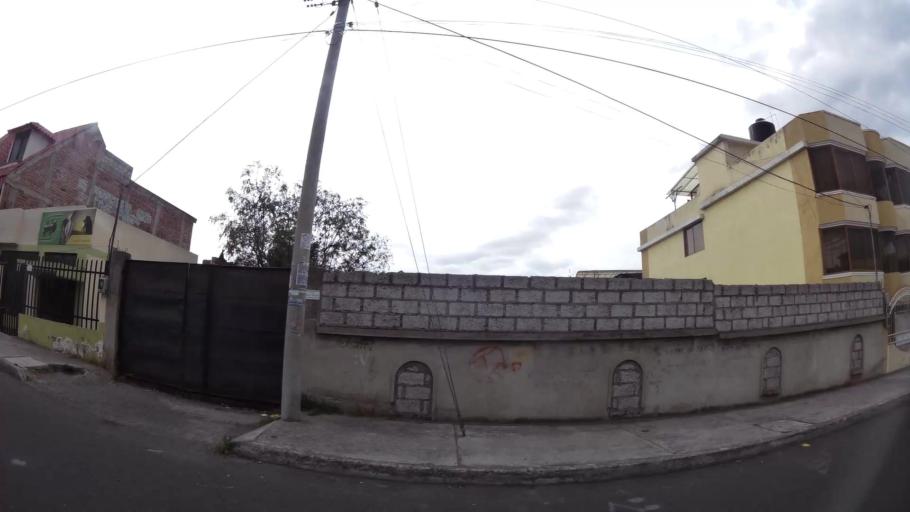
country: EC
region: Tungurahua
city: Ambato
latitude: -1.2737
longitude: -78.6280
